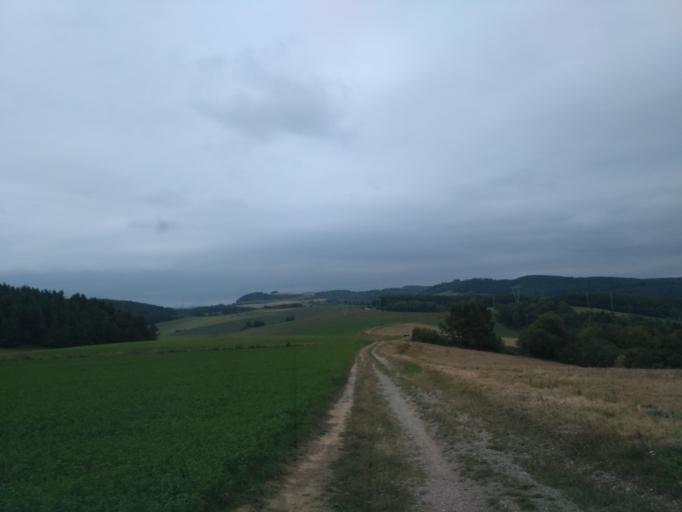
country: SK
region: Presovsky
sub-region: Okres Presov
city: Presov
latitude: 48.9003
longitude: 21.1634
